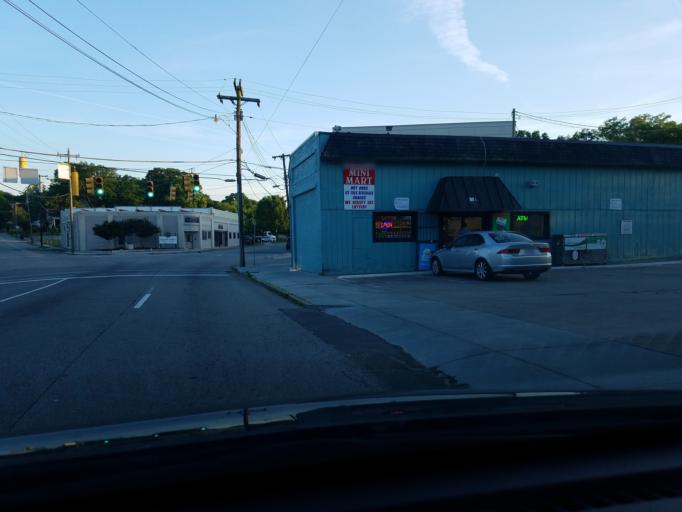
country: US
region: North Carolina
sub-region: Durham County
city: Durham
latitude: 36.0016
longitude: -78.8953
